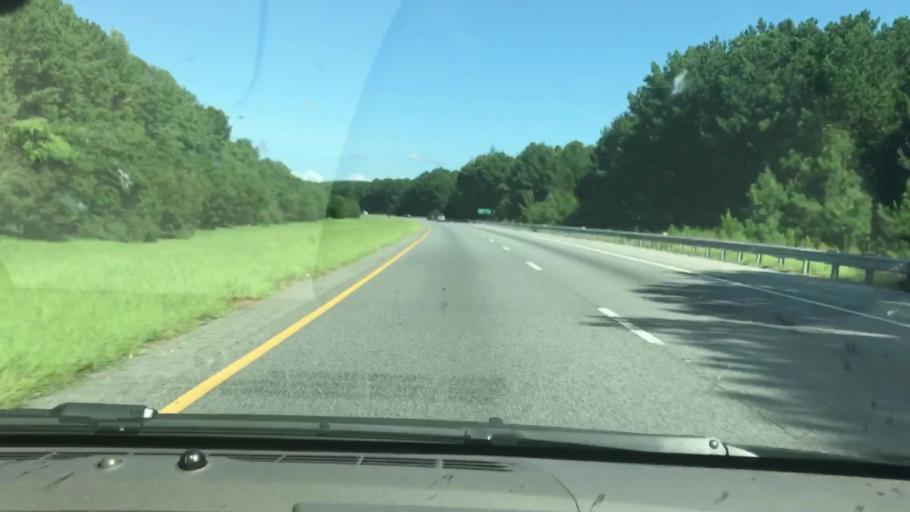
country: US
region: Alabama
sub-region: Russell County
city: Phenix City
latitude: 32.6159
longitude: -84.9506
